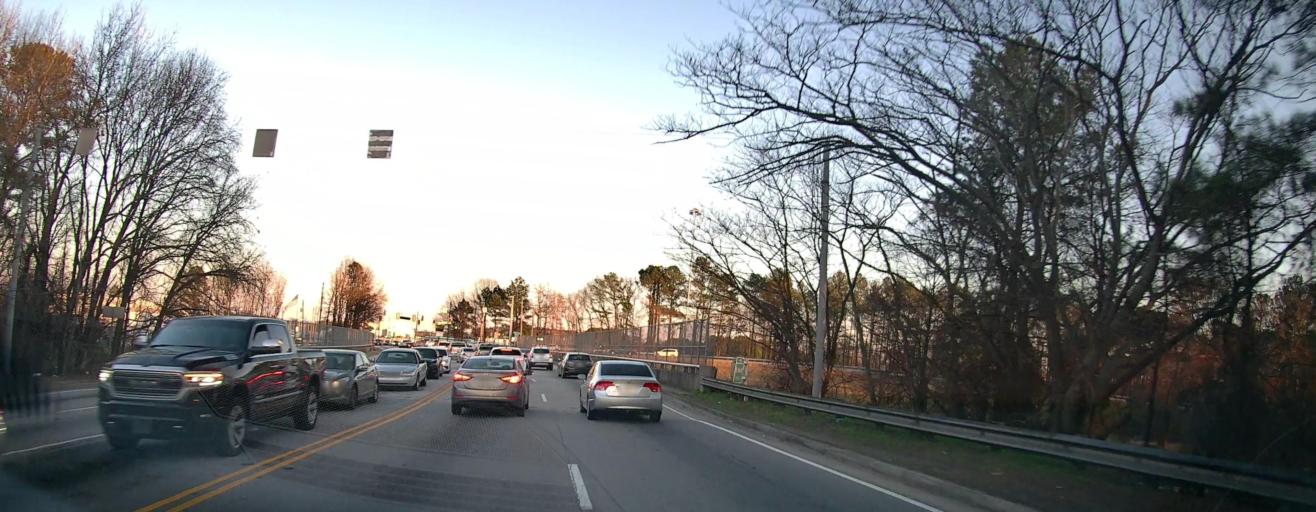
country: US
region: Georgia
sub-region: Fulton County
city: Union City
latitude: 33.5672
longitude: -84.5347
